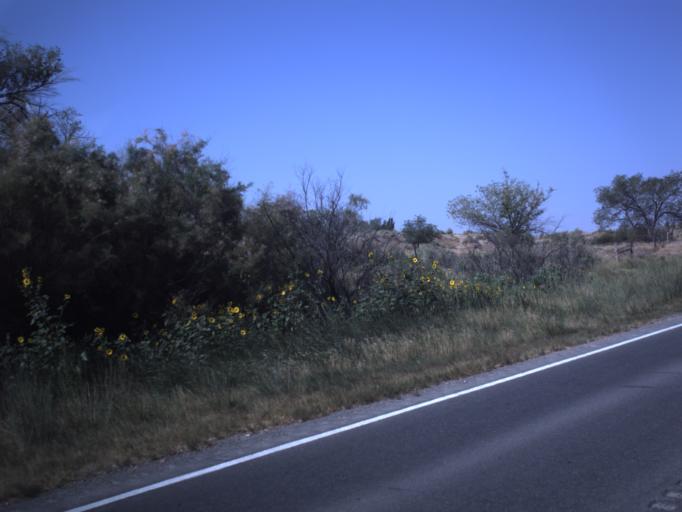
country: US
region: Utah
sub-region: Uintah County
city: Naples
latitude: 40.3694
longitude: -109.3750
